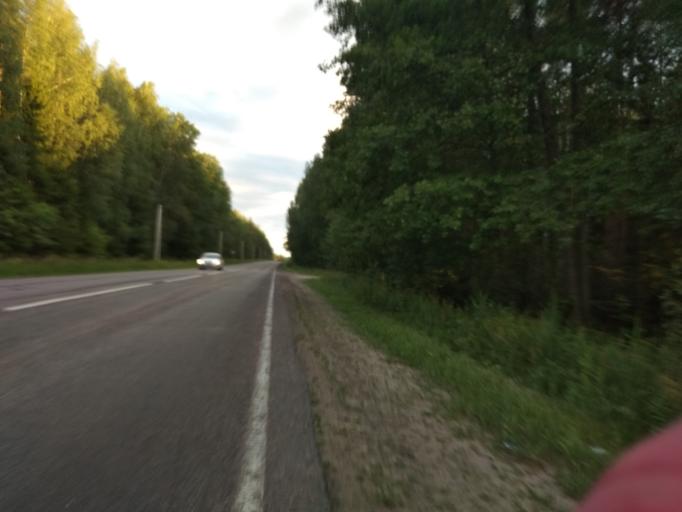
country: RU
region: Moskovskaya
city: Misheronskiy
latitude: 55.6164
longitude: 39.7237
